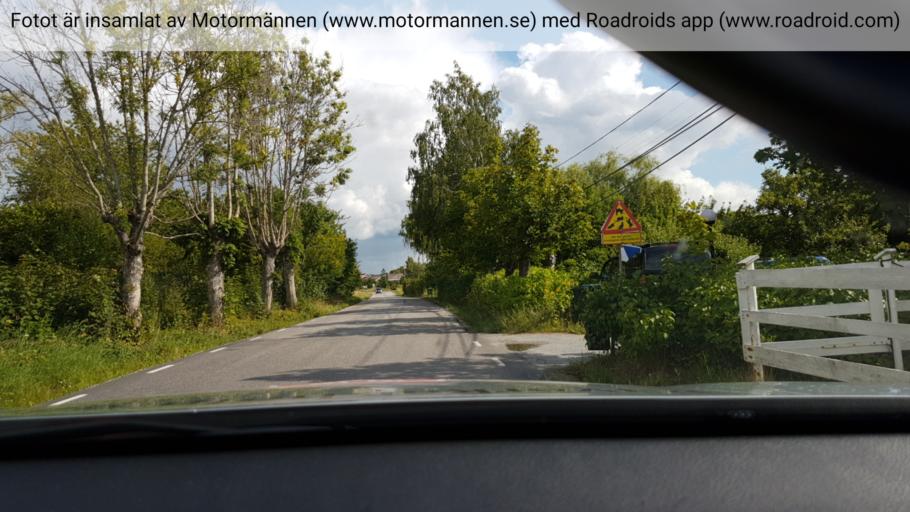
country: SE
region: Stockholm
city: Stenhamra
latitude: 59.3992
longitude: 17.6489
